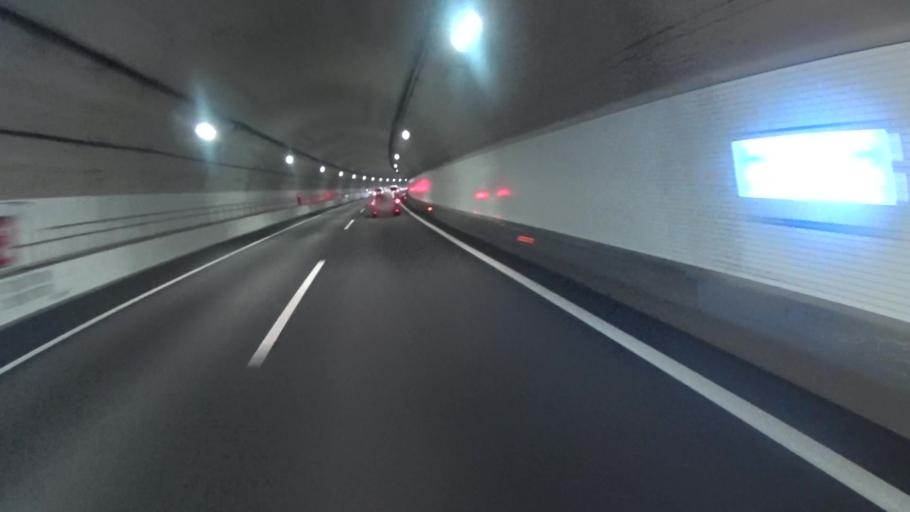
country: JP
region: Mie
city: Kameyama
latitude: 34.9172
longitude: 136.4207
